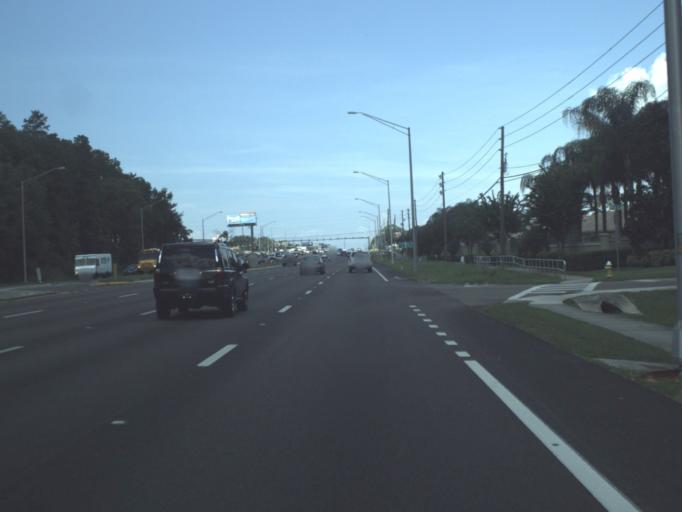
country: US
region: Florida
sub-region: Pinellas County
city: Tarpon Springs
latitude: 28.1188
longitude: -82.7398
